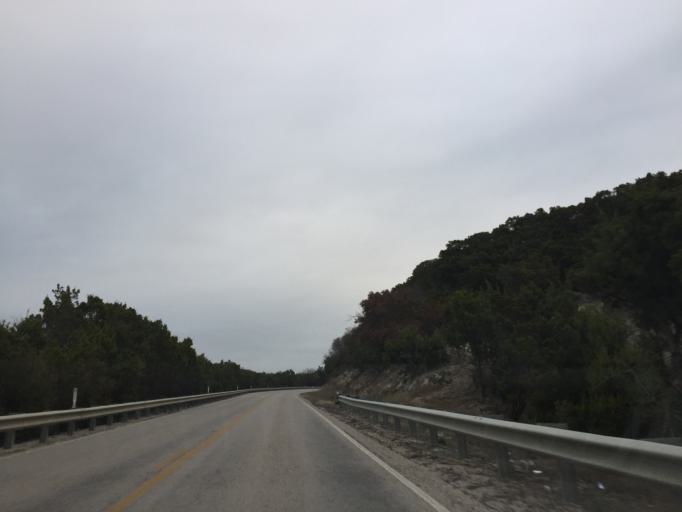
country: US
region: Texas
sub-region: Coryell County
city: Ames
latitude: 31.5036
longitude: -97.7275
